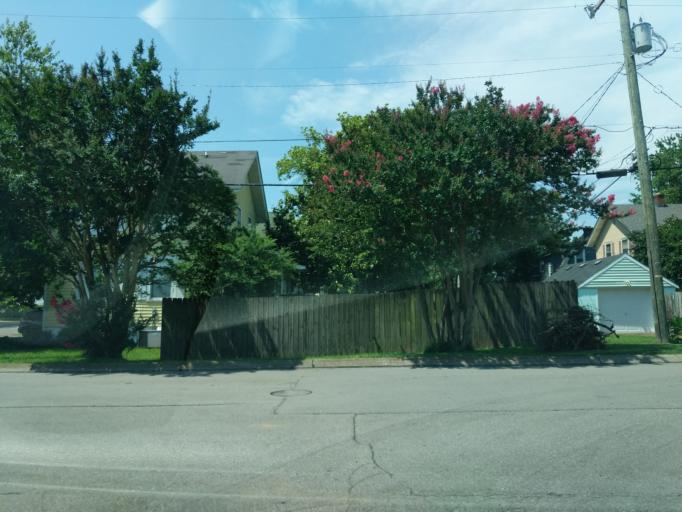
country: US
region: Tennessee
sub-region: Davidson County
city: Lakewood
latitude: 36.2607
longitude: -86.6459
